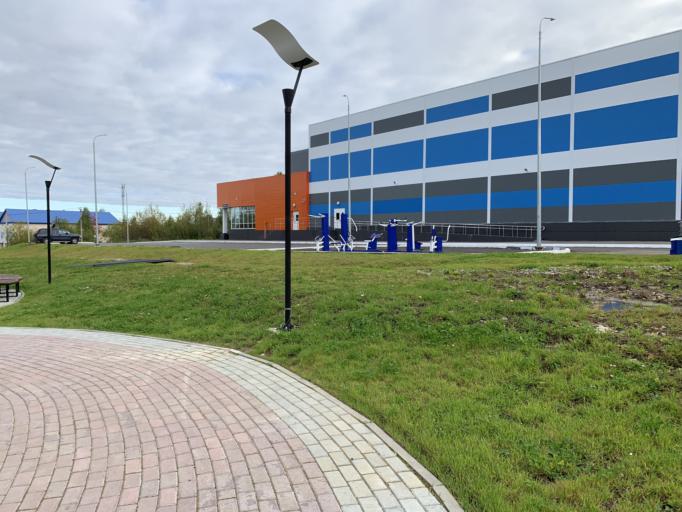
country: RU
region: Perm
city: Gubakha
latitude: 58.8334
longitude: 57.5611
